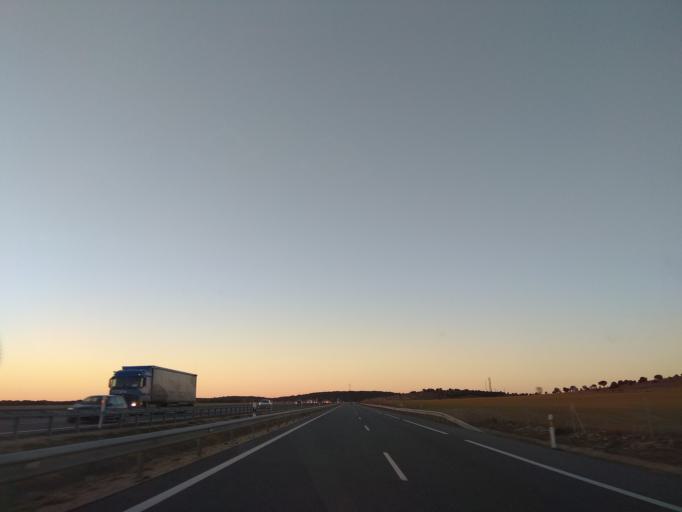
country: ES
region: Castille and Leon
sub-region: Provincia de Burgos
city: Quintanilla de la Mata
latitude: 41.9614
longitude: -3.7724
